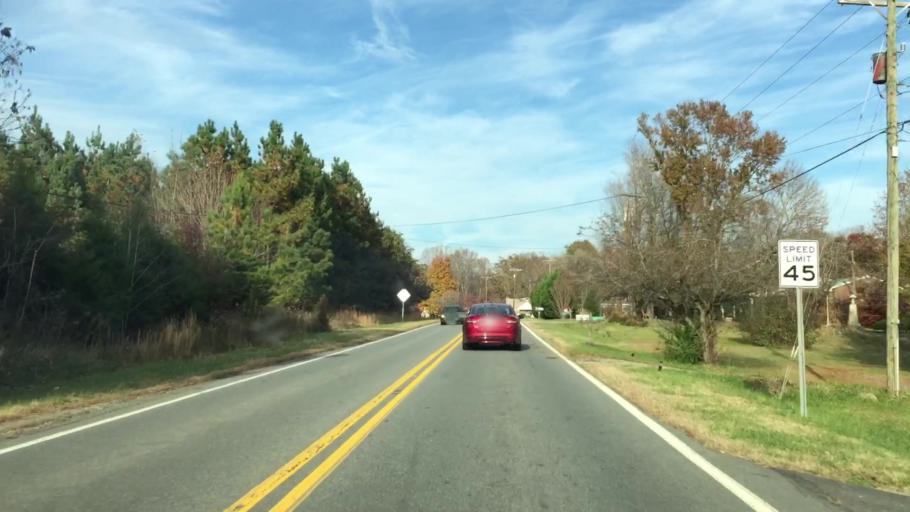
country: US
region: North Carolina
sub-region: Rockingham County
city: Reidsville
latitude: 36.3114
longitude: -79.7172
